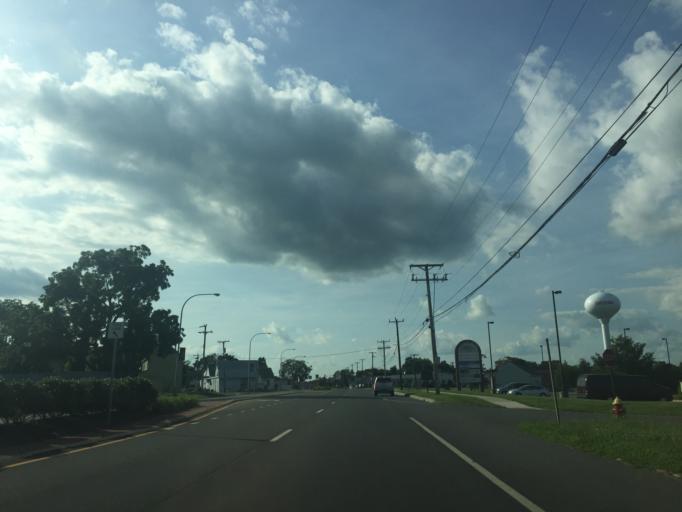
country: US
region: Delaware
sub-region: Kent County
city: Smyrna
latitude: 39.2987
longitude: -75.6008
